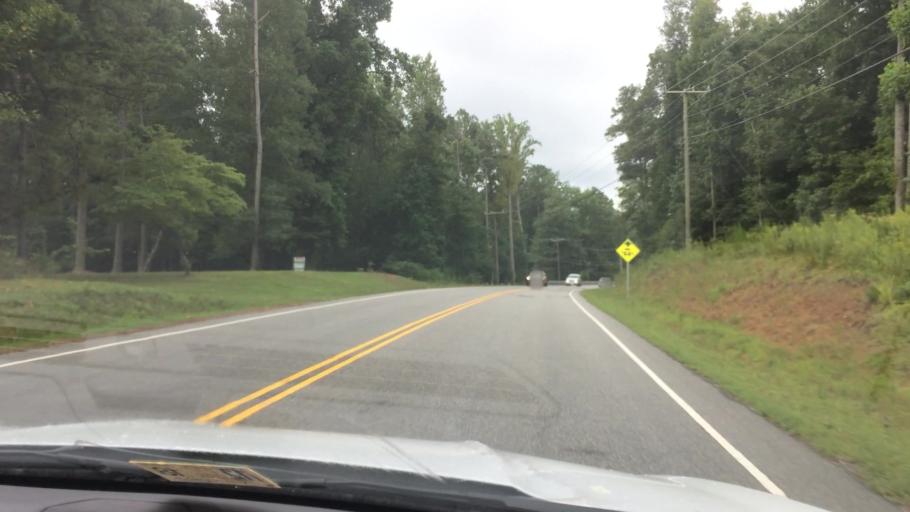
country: US
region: Virginia
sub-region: New Kent County
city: New Kent
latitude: 37.4526
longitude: -77.0370
